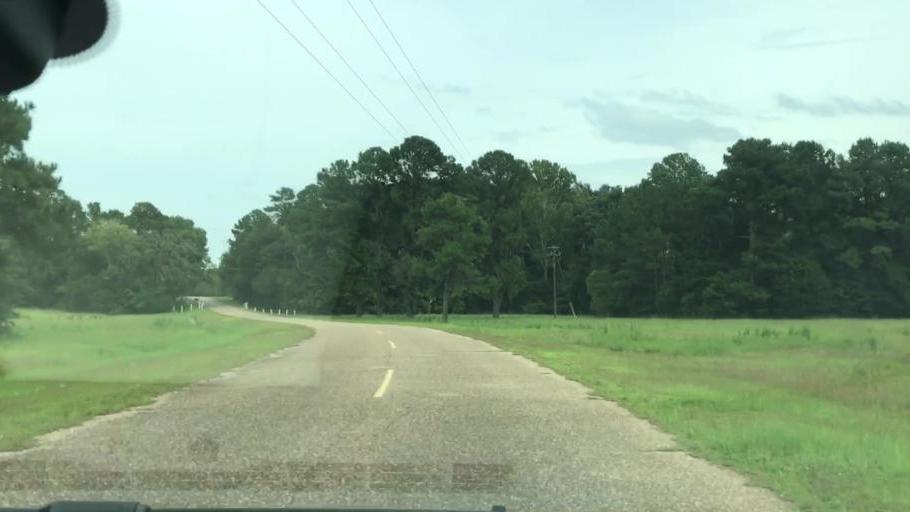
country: US
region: Georgia
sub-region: Clay County
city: Fort Gaines
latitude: 31.6270
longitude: -85.0559
